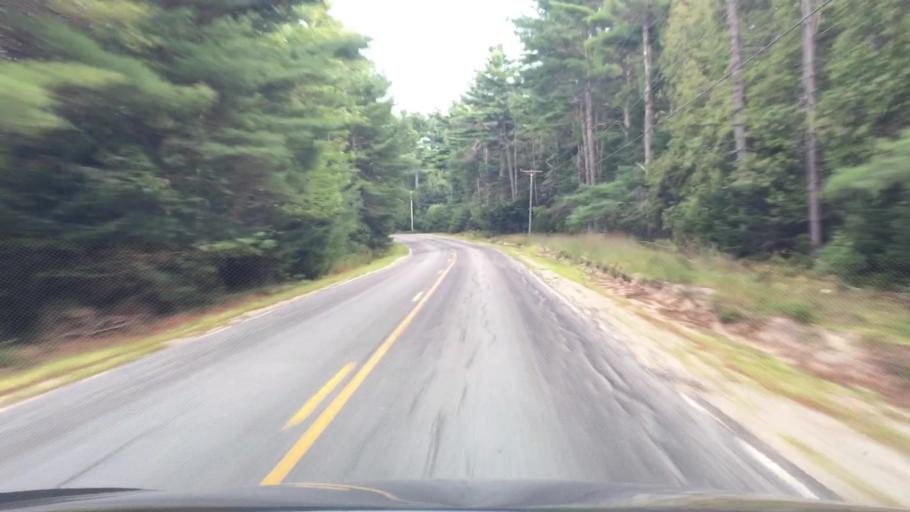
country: US
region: Maine
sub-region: Hancock County
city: Surry
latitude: 44.5085
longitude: -68.5971
